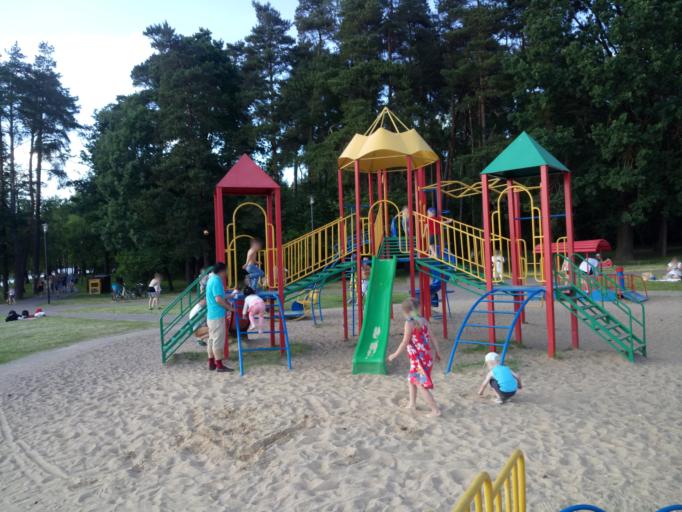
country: BY
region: Minsk
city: Zhdanovichy
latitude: 53.9461
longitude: 27.4865
